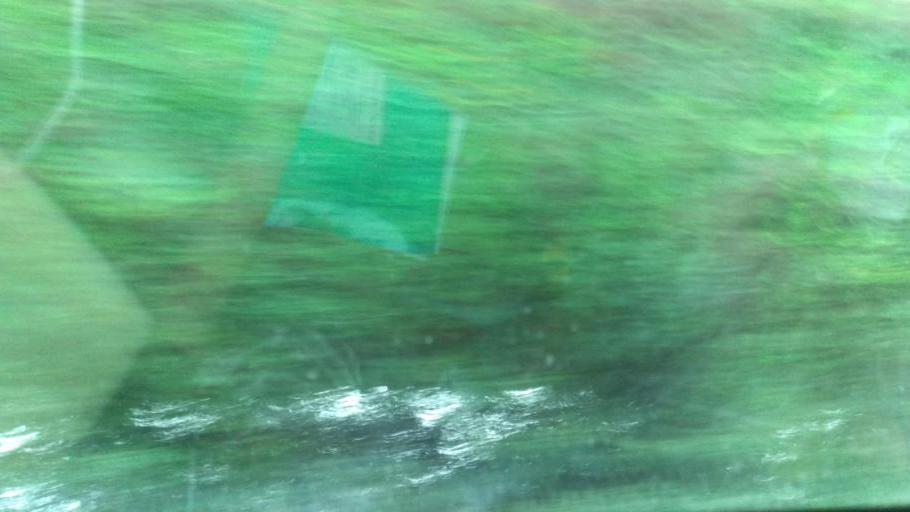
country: BR
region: Pernambuco
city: Garanhuns
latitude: -8.8751
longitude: -36.5196
